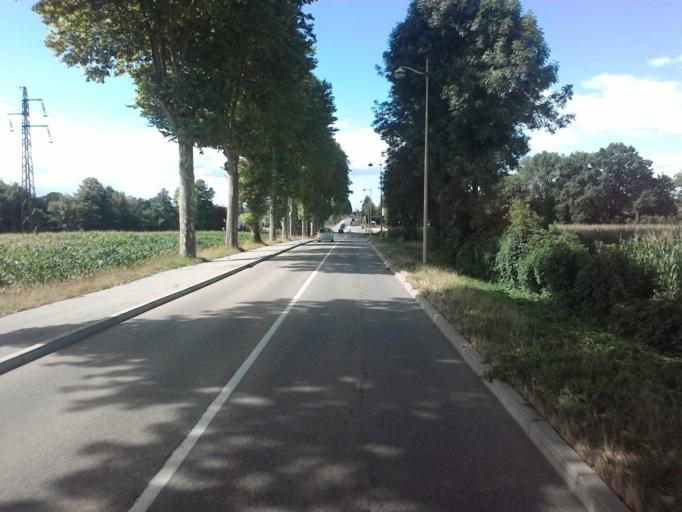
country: FR
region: Rhone-Alpes
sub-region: Departement de l'Ain
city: Ambronay
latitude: 46.0009
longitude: 5.3577
